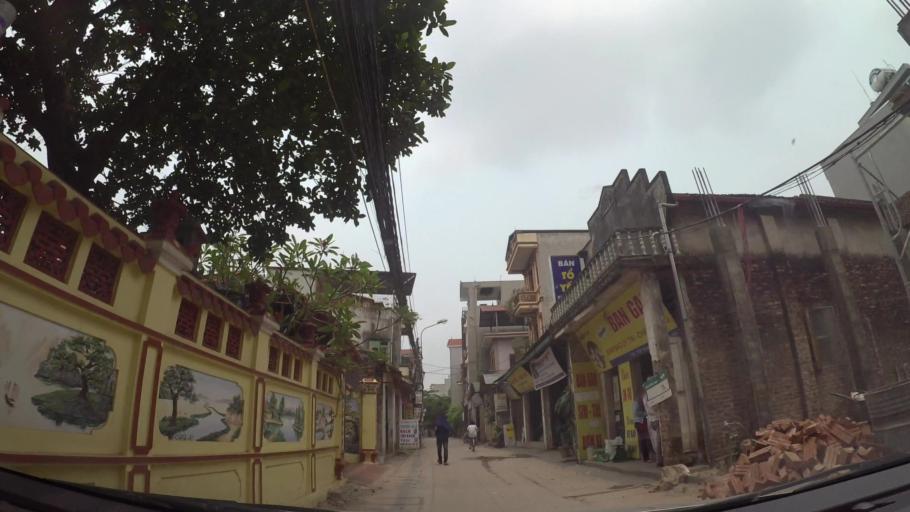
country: VN
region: Ha Noi
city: Ha Dong
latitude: 20.9824
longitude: 105.7488
